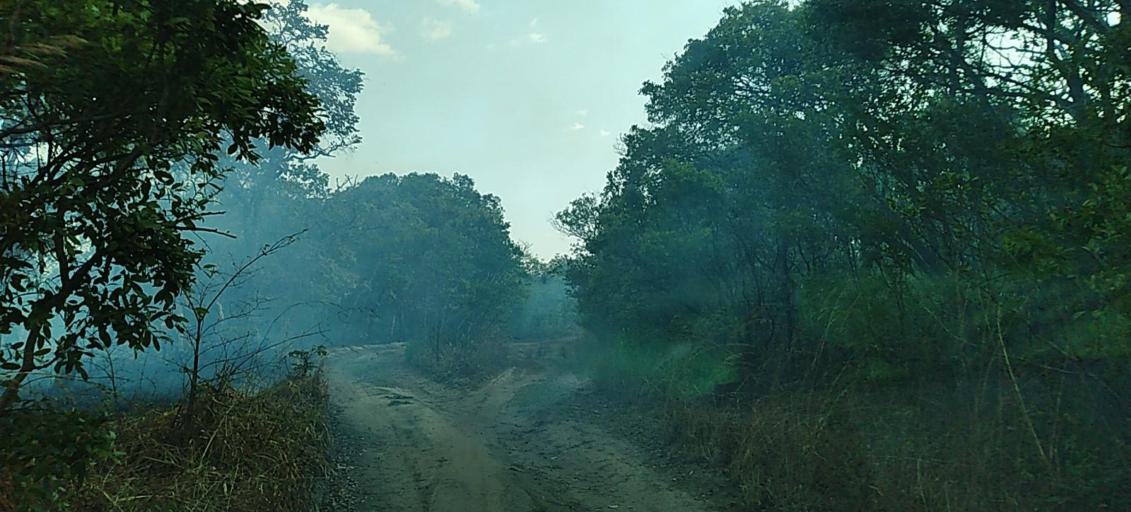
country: ZM
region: North-Western
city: Mwinilunga
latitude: -11.3262
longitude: 24.7381
